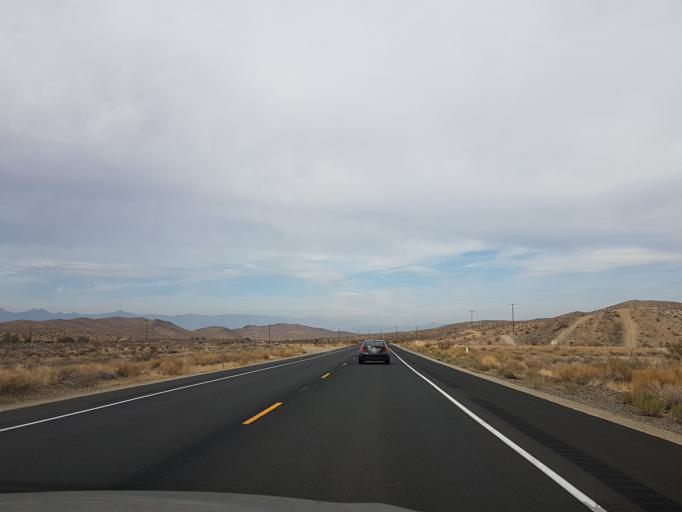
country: US
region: California
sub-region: Kern County
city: Ridgecrest
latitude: 35.5186
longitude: -117.6725
